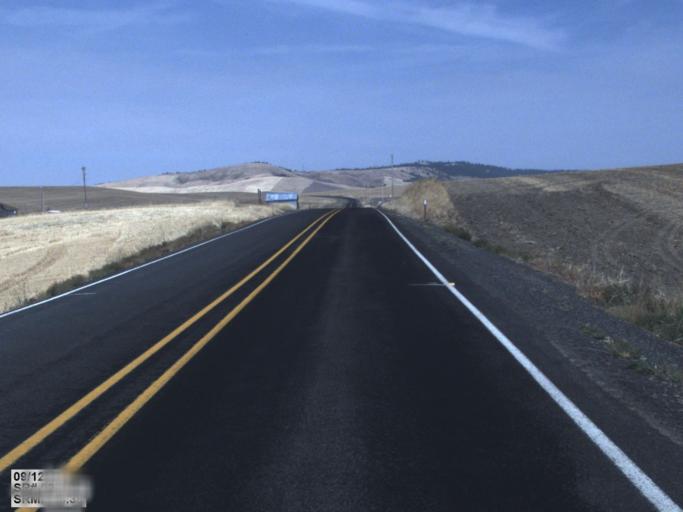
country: US
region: Idaho
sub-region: Benewah County
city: Plummer
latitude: 47.2652
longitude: -117.1311
